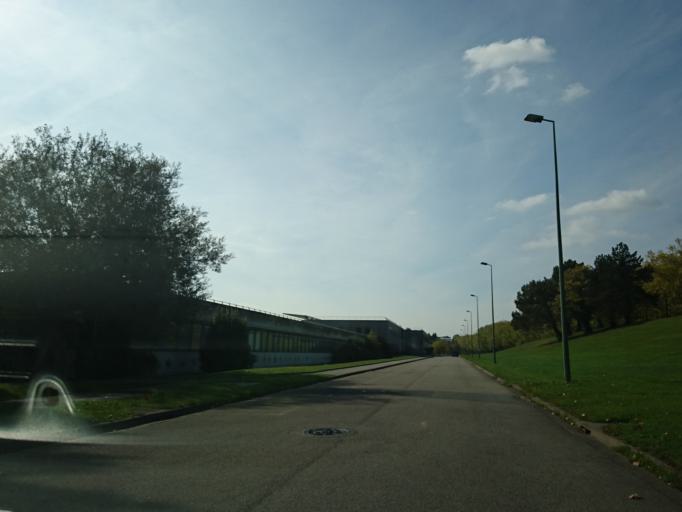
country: FR
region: Brittany
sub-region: Departement d'Ille-et-Vilaine
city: Rennes
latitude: 48.1215
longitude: -1.6395
